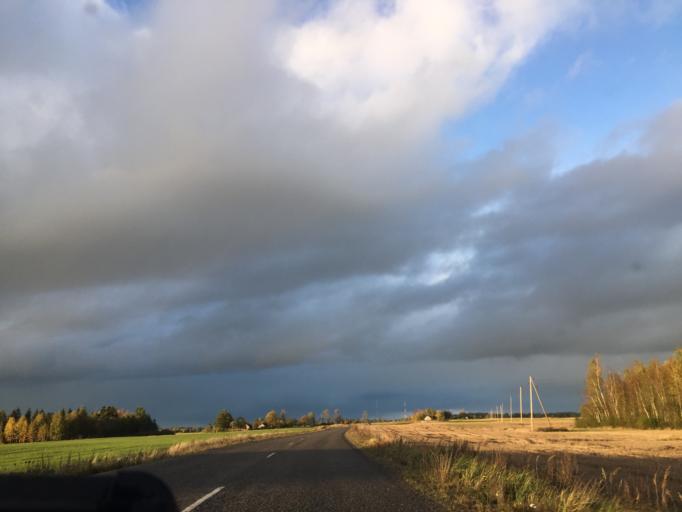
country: LV
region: Talsu Rajons
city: Sabile
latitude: 56.9252
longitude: 22.3962
